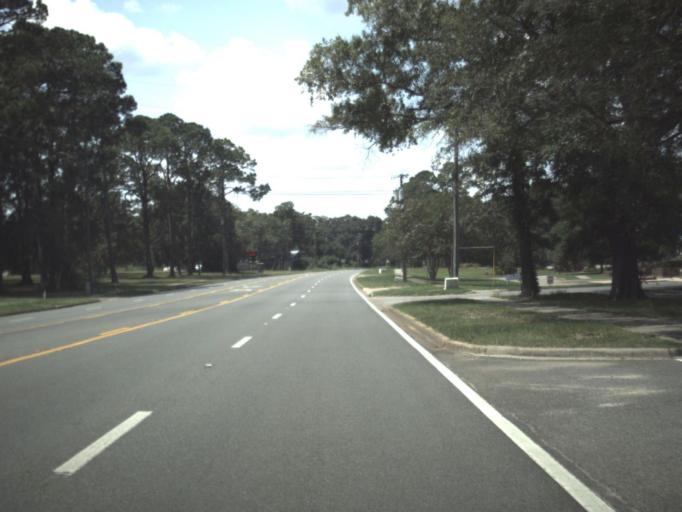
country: US
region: Florida
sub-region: Washington County
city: Chipley
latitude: 30.7773
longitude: -85.5516
